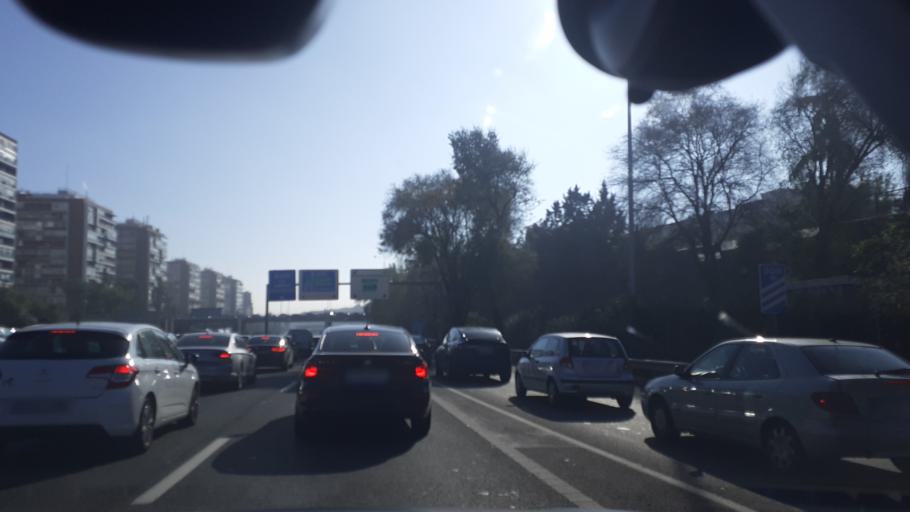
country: ES
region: Madrid
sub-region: Provincia de Madrid
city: Ciudad Lineal
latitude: 40.4379
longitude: -3.6598
